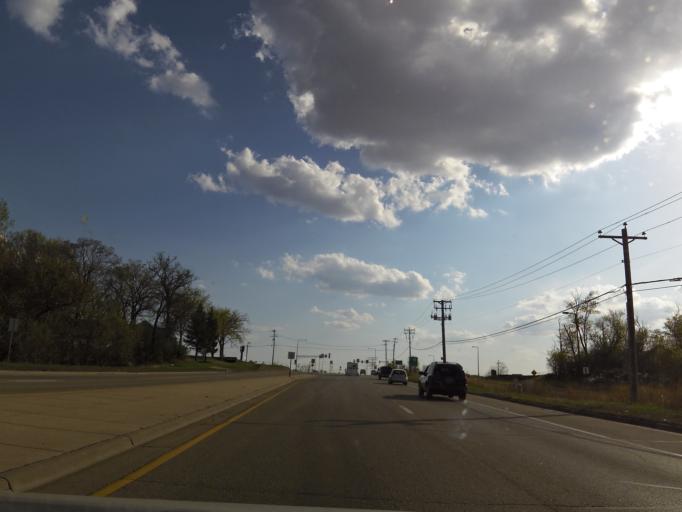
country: US
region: Minnesota
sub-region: Washington County
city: Stillwater
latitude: 45.0387
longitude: -92.8440
